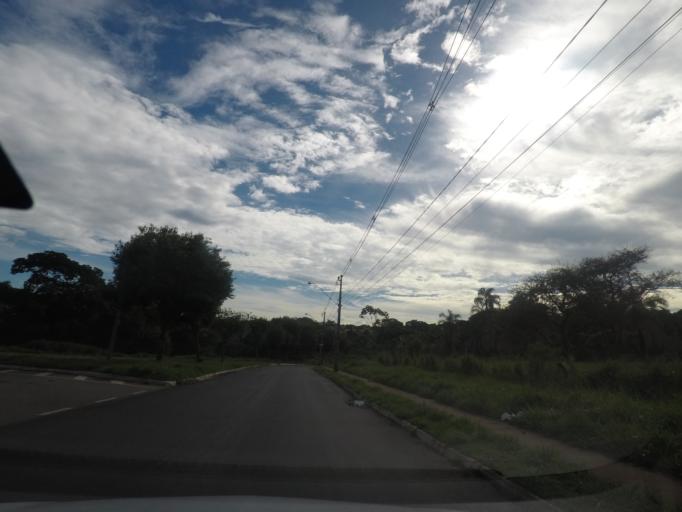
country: BR
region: Goias
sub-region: Aparecida De Goiania
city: Aparecida de Goiania
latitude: -16.8184
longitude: -49.3048
